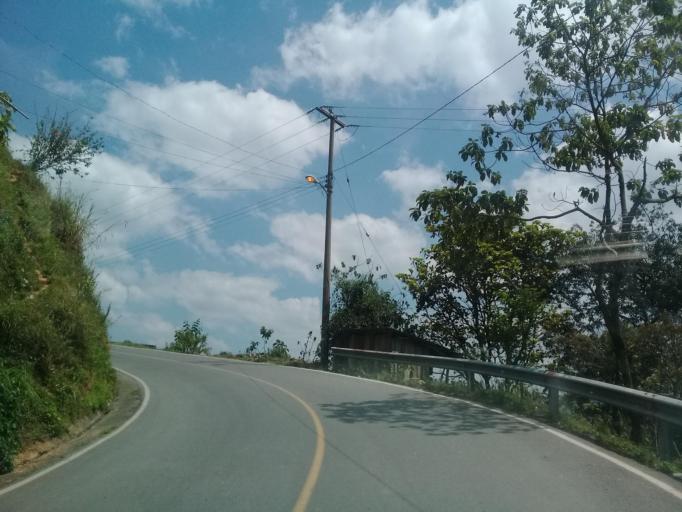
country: MX
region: Veracruz
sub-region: Tlilapan
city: Tonalixco
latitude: 18.7870
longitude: -97.0599
